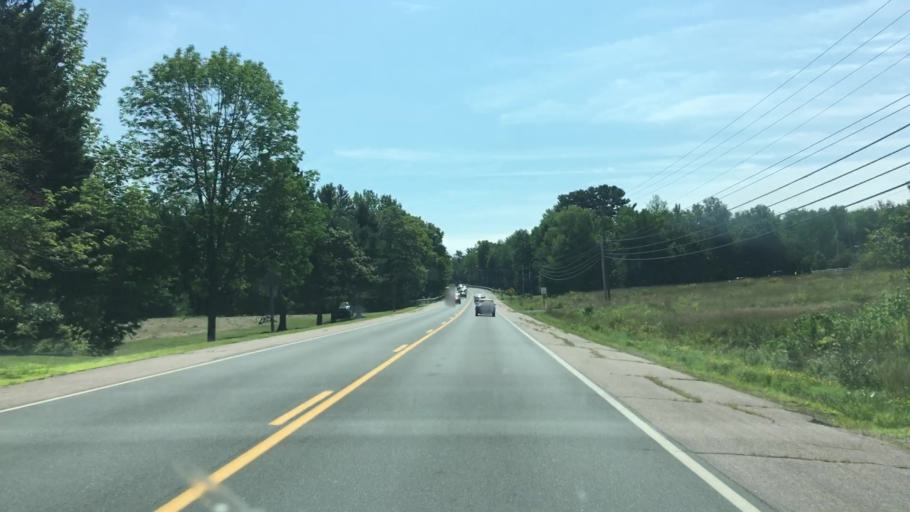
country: US
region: Maine
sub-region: Washington County
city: Calais
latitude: 45.1647
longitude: -67.2385
